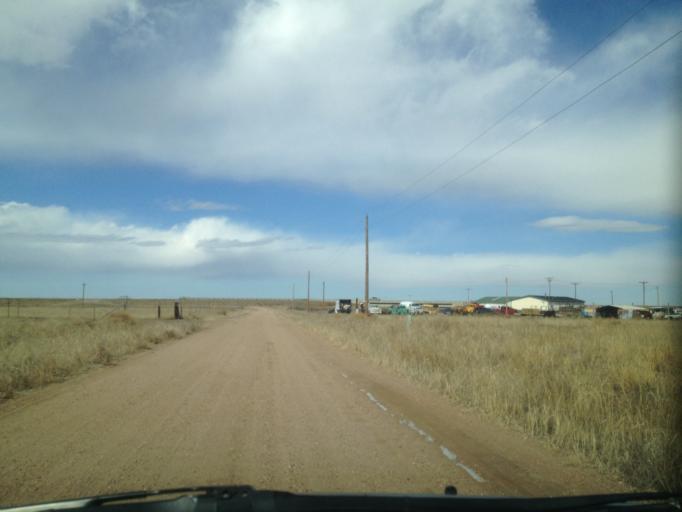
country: US
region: Colorado
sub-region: Weld County
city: Keenesburg
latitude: 40.2887
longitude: -104.2555
